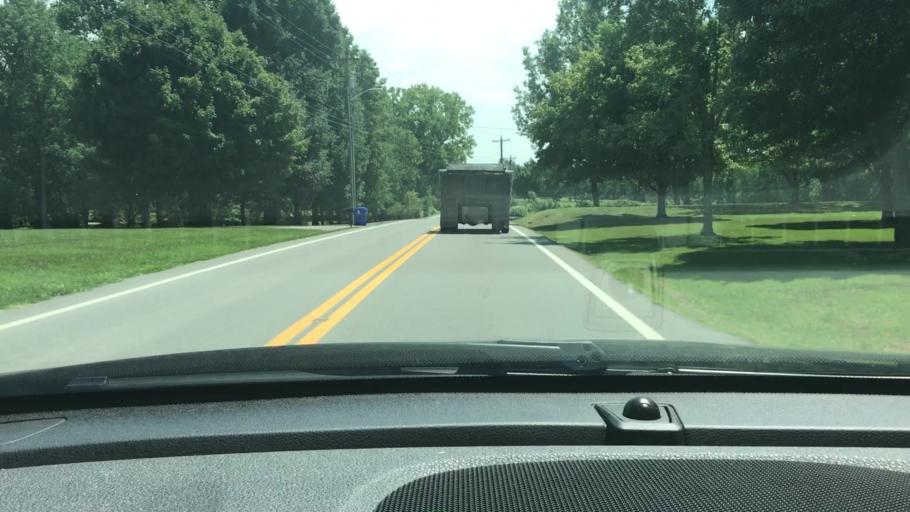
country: US
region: Tennessee
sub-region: Sumner County
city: White House
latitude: 36.4456
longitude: -86.6448
